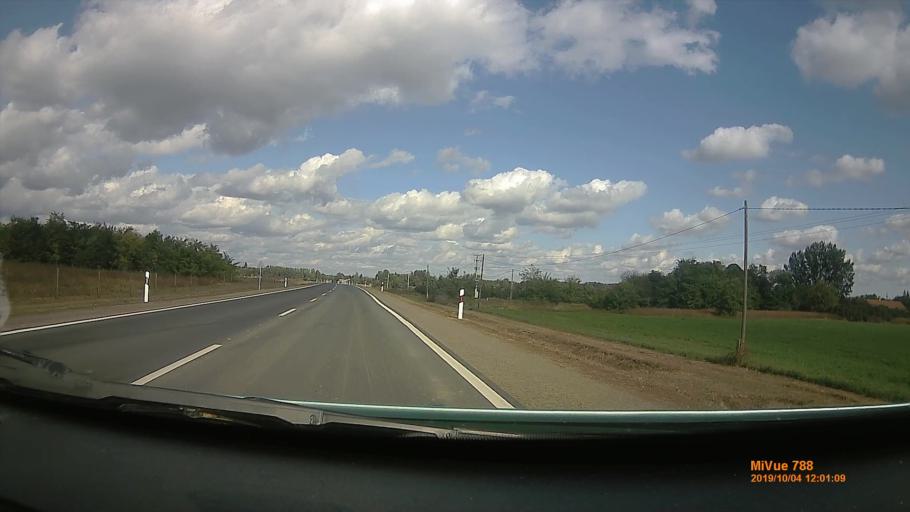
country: HU
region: Szabolcs-Szatmar-Bereg
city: Nyirtelek
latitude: 48.0163
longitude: 21.6788
